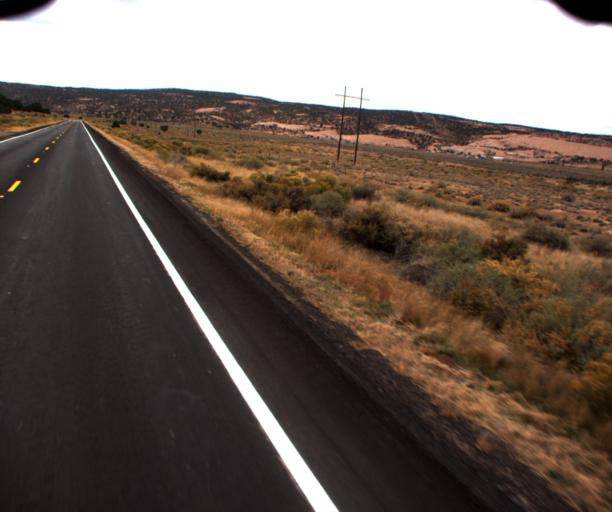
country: US
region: Arizona
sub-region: Navajo County
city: Kayenta
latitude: 36.6181
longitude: -110.4666
